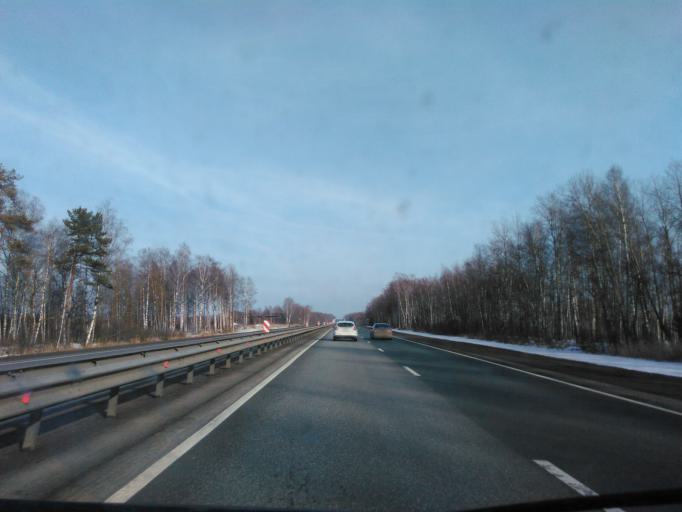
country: RU
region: Smolensk
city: Kholm-Zhirkovskiy
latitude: 55.1851
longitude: 33.7127
